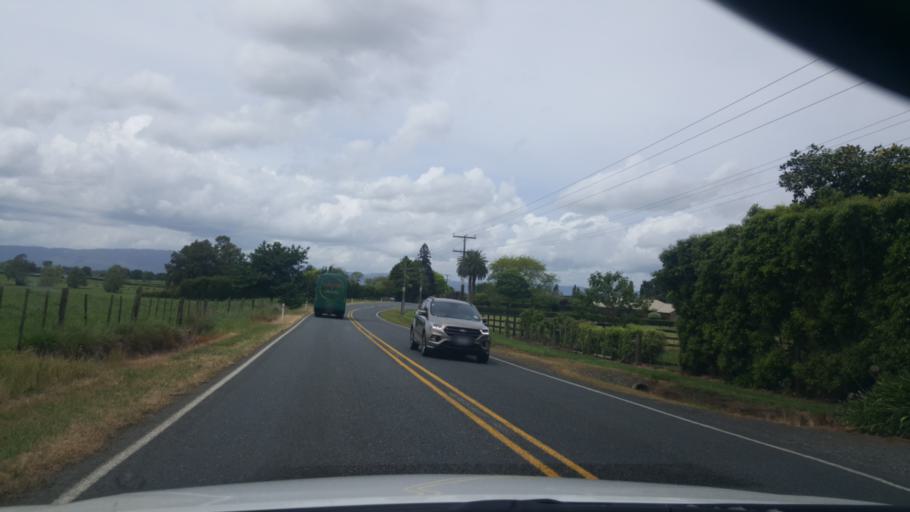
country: NZ
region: Waikato
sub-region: Matamata-Piako District
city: Matamata
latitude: -37.8778
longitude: 175.7058
